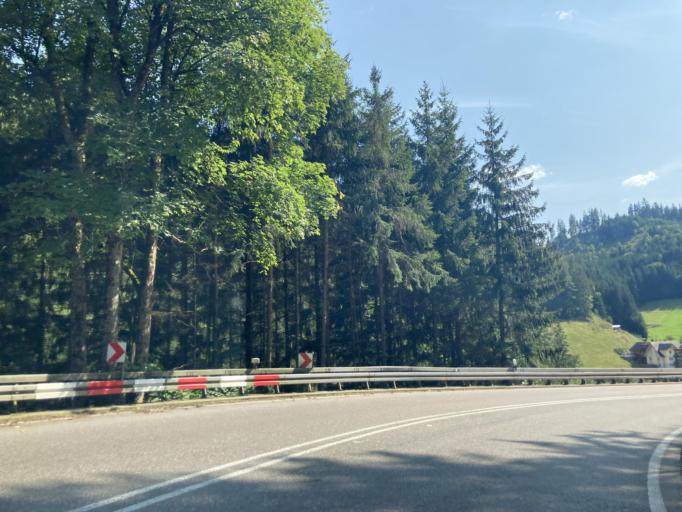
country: DE
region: Baden-Wuerttemberg
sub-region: Freiburg Region
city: Triberg im Schwarzwald
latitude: 48.1355
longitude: 8.2756
